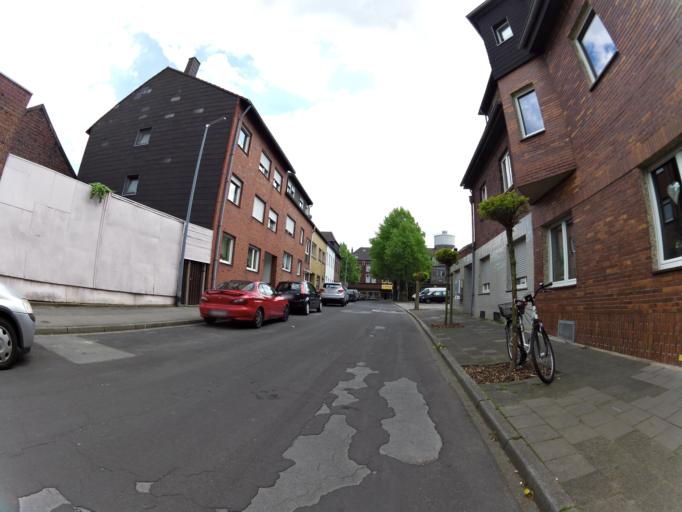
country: DE
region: North Rhine-Westphalia
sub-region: Regierungsbezirk Koln
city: Alsdorf
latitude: 50.8771
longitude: 6.1633
